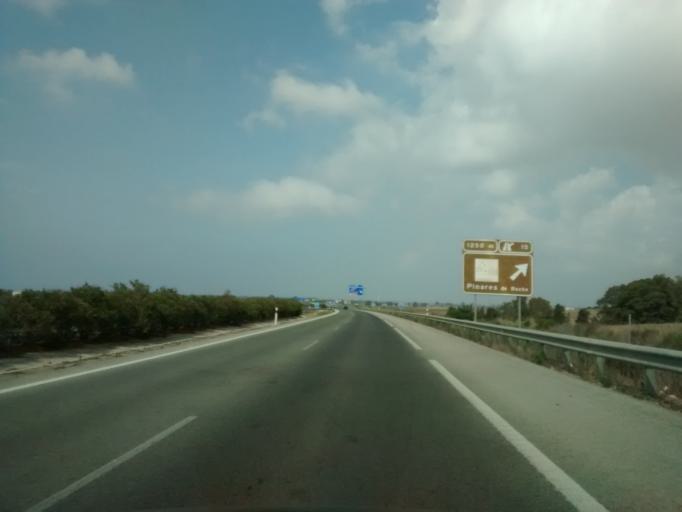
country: ES
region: Andalusia
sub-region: Provincia de Cadiz
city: Conil de la Frontera
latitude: 36.3554
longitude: -6.0844
